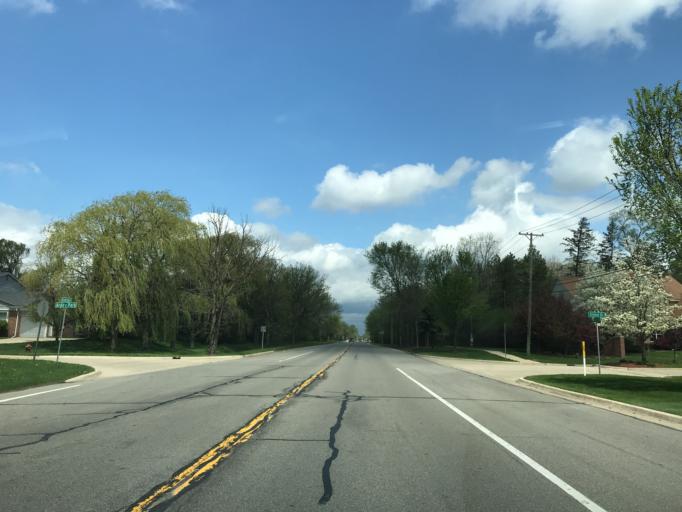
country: US
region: Michigan
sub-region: Oakland County
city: Franklin
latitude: 42.4764
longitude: -83.3184
